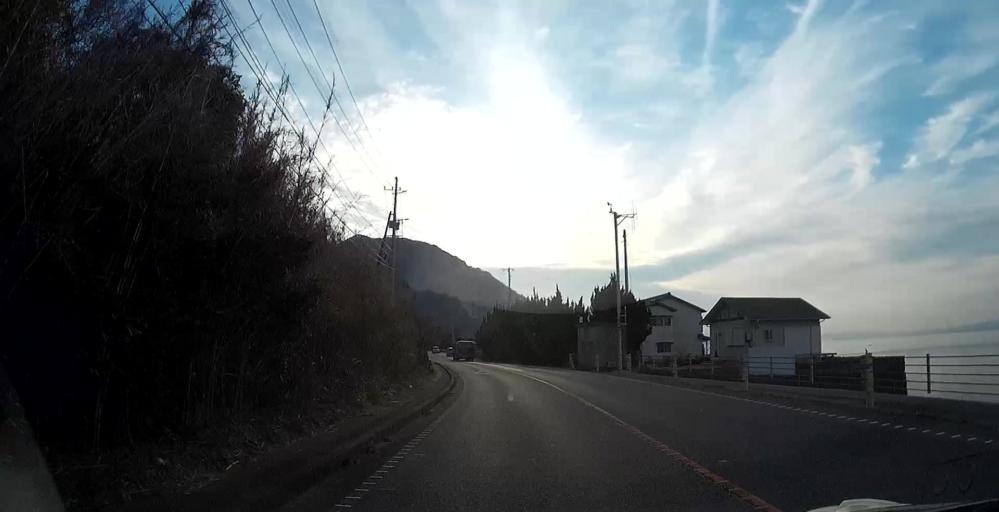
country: JP
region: Nagasaki
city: Shimabara
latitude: 32.6427
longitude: 130.4801
